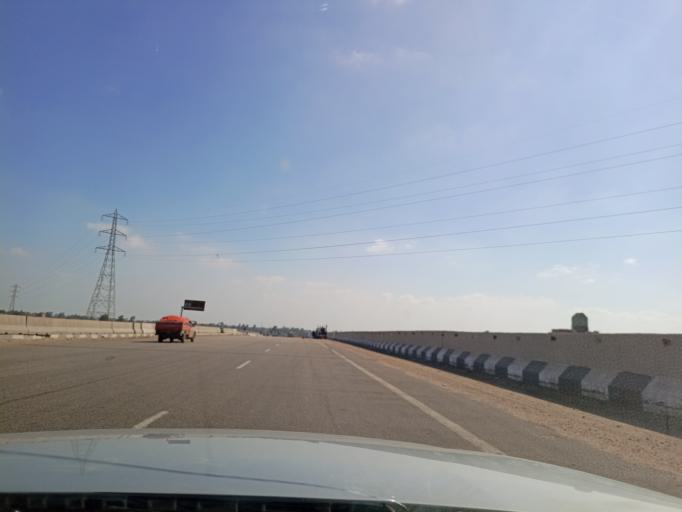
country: EG
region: Eastern Province
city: Mashtul as Suq
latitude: 30.4602
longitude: 31.3323
